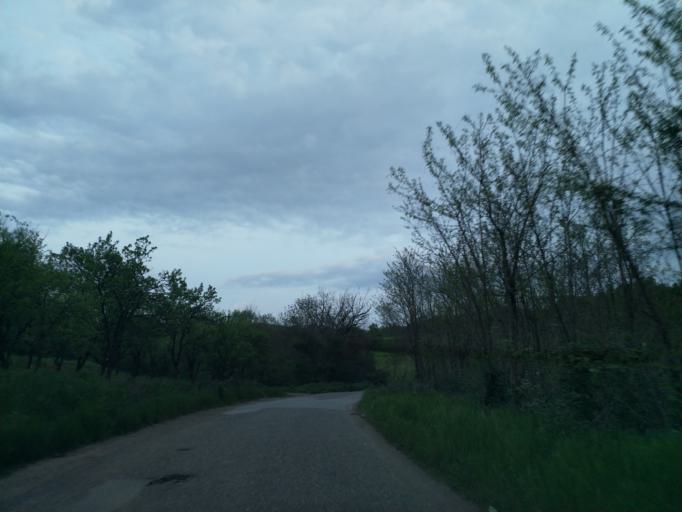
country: RS
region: Central Serbia
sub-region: Pomoravski Okrug
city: Cuprija
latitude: 43.9541
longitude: 21.4828
